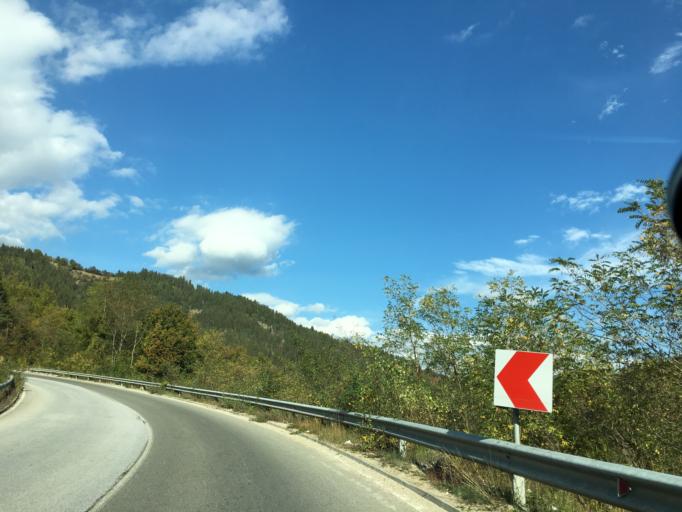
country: BG
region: Smolyan
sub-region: Obshtina Madan
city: Madan
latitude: 41.5353
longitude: 24.9209
